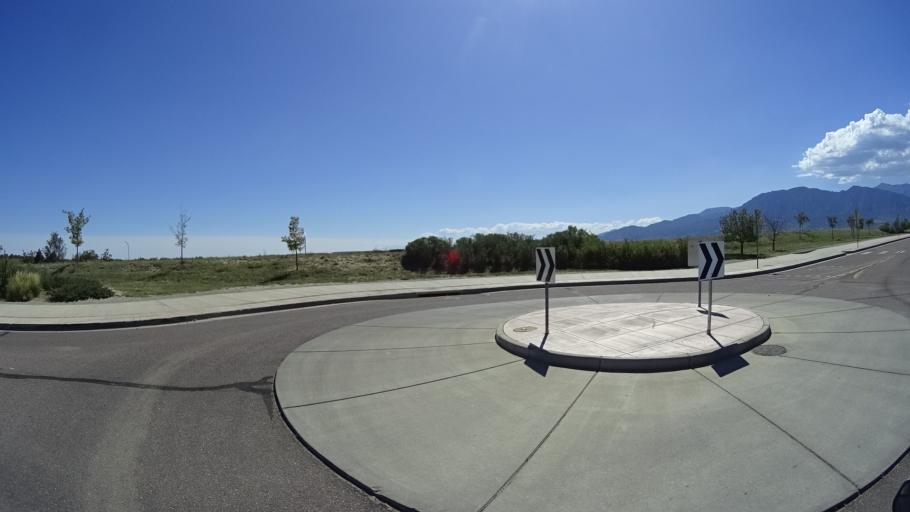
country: US
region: Colorado
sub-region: El Paso County
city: Stratmoor
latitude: 38.7818
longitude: -104.7473
